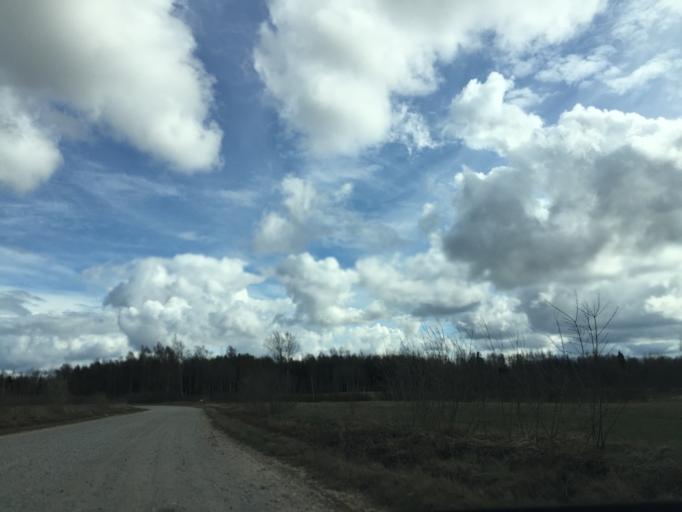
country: LV
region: Limbazu Rajons
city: Limbazi
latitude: 57.6103
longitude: 24.7849
